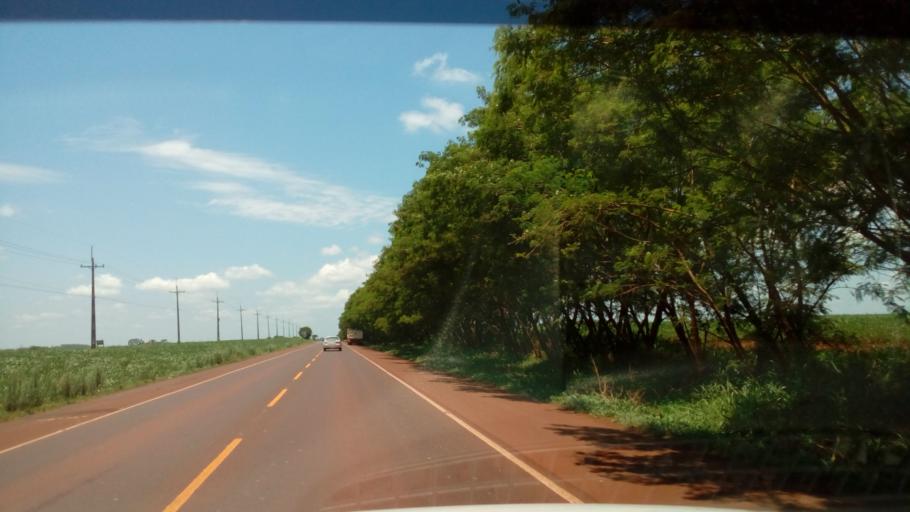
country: PY
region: Alto Parana
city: Naranjal
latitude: -25.9426
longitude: -55.1204
